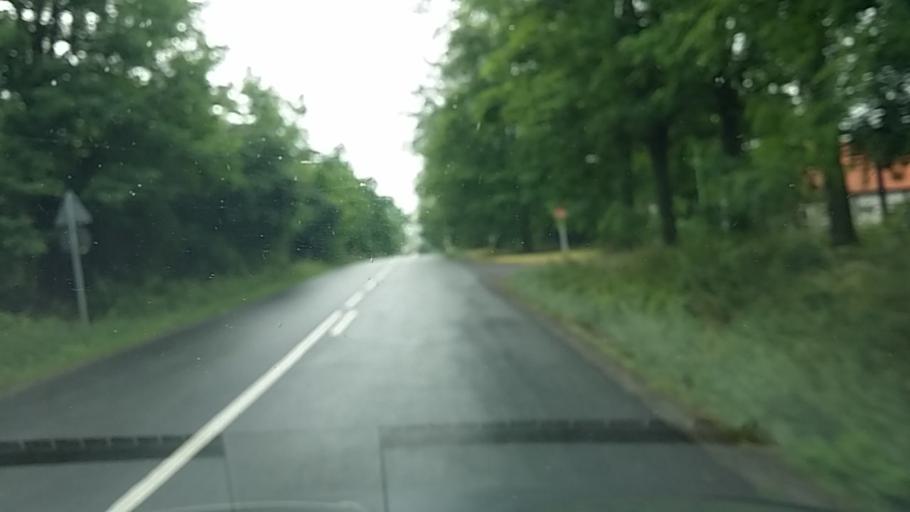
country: HU
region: Pest
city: Szob
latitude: 47.9438
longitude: 18.7778
